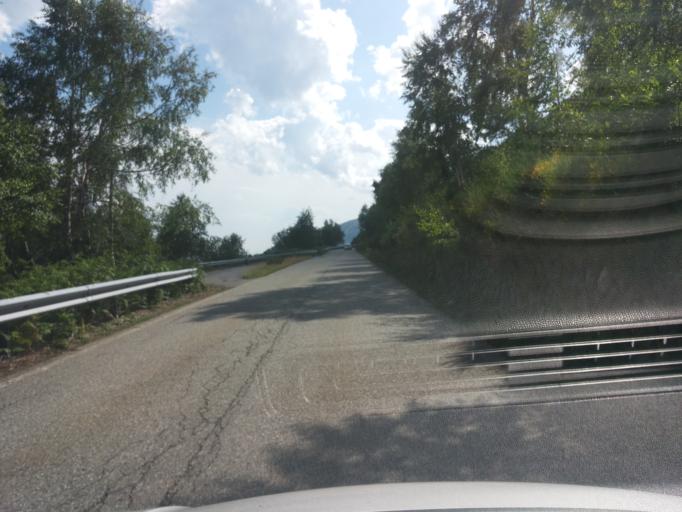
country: IT
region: Piedmont
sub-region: Provincia di Biella
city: Sagliano Micca
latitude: 45.6561
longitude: 8.0512
